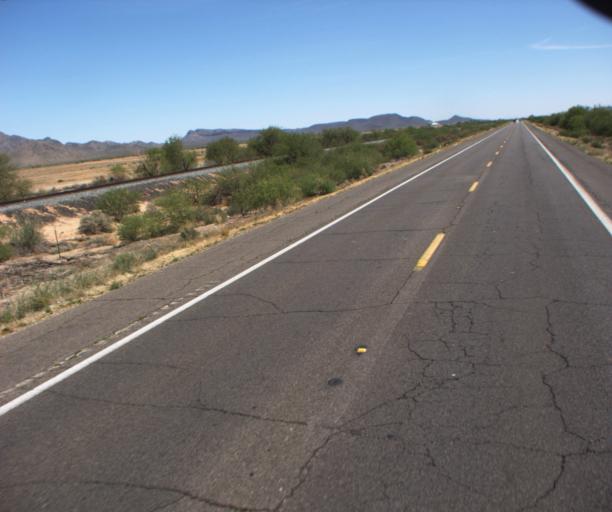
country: US
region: Arizona
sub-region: Maricopa County
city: Sun Lakes
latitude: 33.1663
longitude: -111.7885
